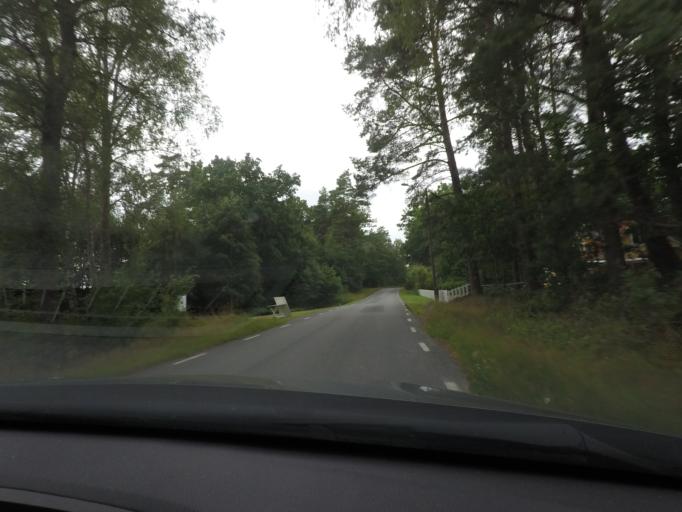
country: SE
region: Kronoberg
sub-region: Markaryds Kommun
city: Markaryd
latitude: 56.3954
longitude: 13.6743
